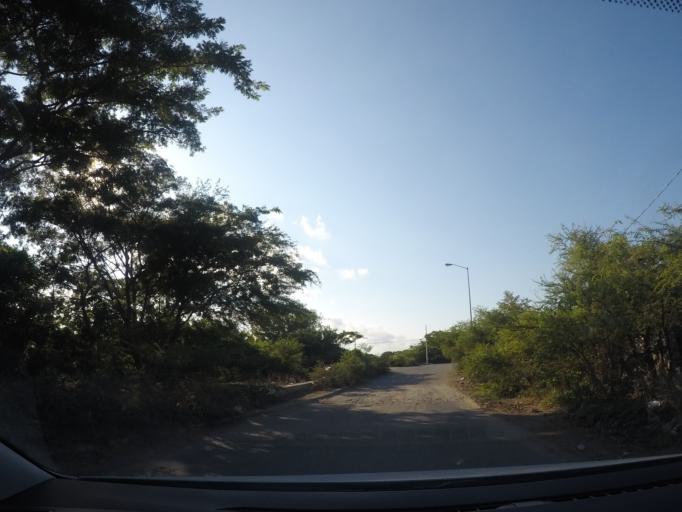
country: MX
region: Oaxaca
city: Juchitan de Zaragoza
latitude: 16.4268
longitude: -95.0315
